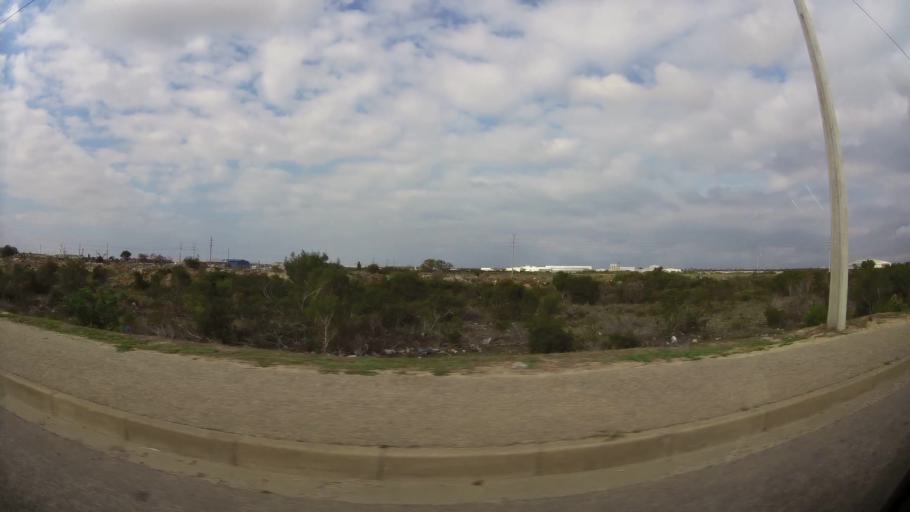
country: ZA
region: Eastern Cape
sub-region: Nelson Mandela Bay Metropolitan Municipality
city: Port Elizabeth
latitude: -33.8066
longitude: 25.6193
